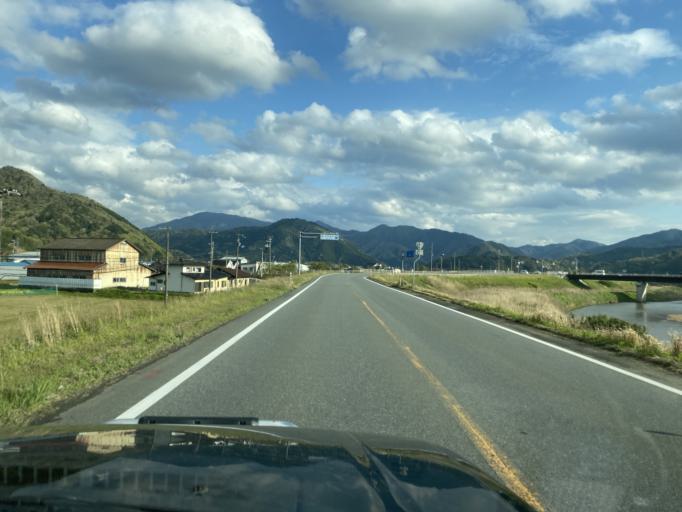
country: JP
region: Hyogo
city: Toyooka
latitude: 35.4827
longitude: 134.8616
